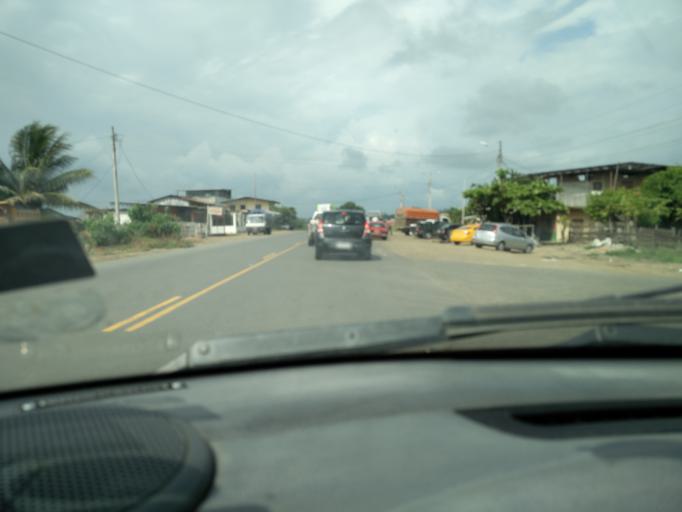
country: EC
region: Manabi
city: Rocafuerte
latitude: -0.9177
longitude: -80.4515
